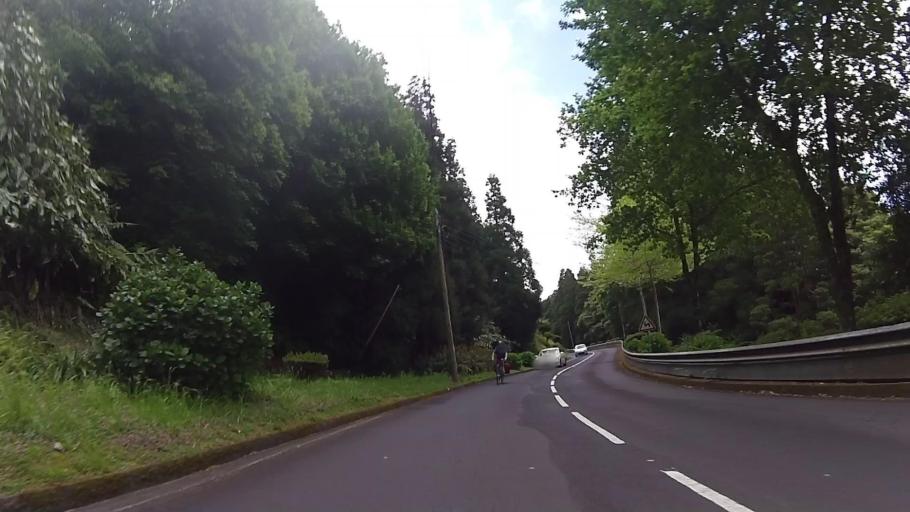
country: PT
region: Azores
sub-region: Povoacao
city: Furnas
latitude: 37.7650
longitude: -25.2885
